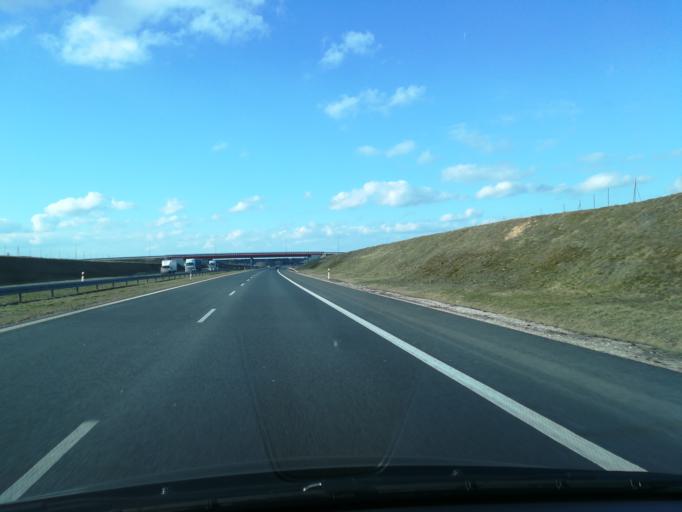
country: PL
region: Lodz Voivodeship
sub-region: Powiat kutnowski
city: Strzelce
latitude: 52.3015
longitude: 19.3730
